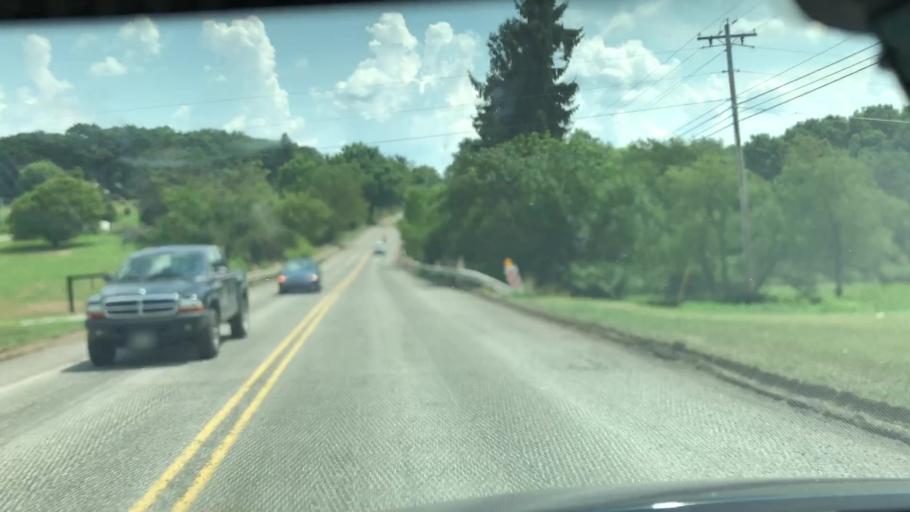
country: US
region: Pennsylvania
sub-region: Butler County
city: Saxonburg
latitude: 40.7881
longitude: -79.8037
